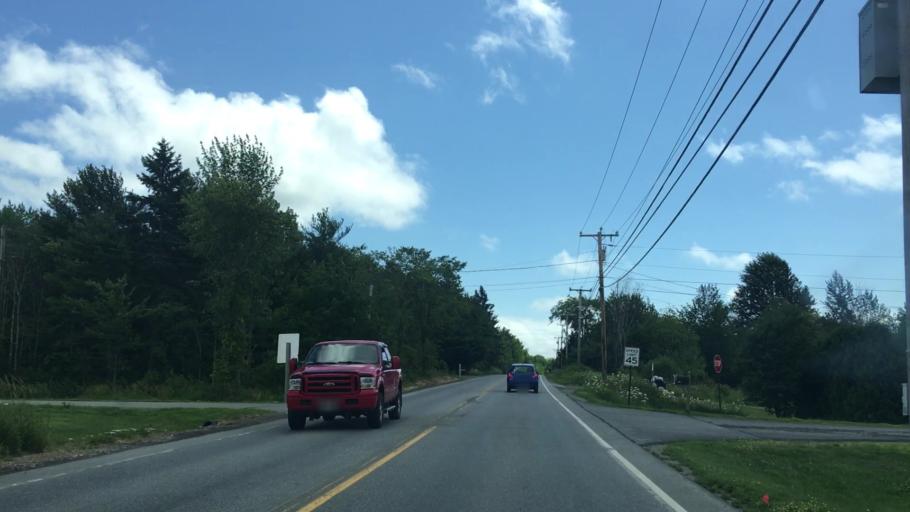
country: US
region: Maine
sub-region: Penobscot County
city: Hermon
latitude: 44.8044
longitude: -68.8993
